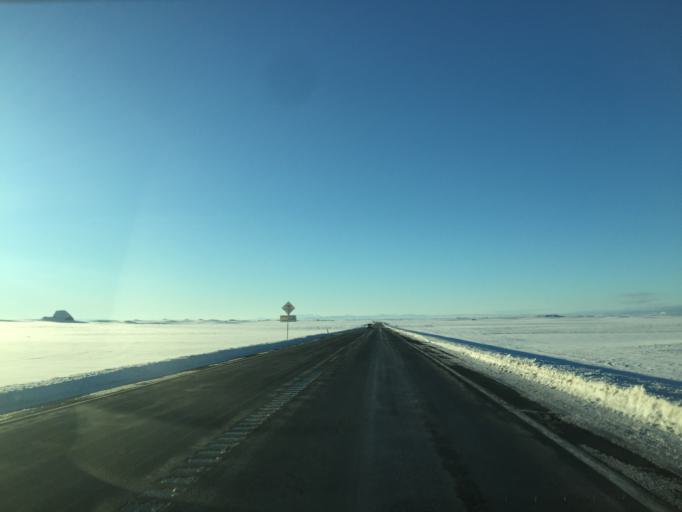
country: US
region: Washington
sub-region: Grant County
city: Soap Lake
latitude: 47.6199
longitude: -119.4293
